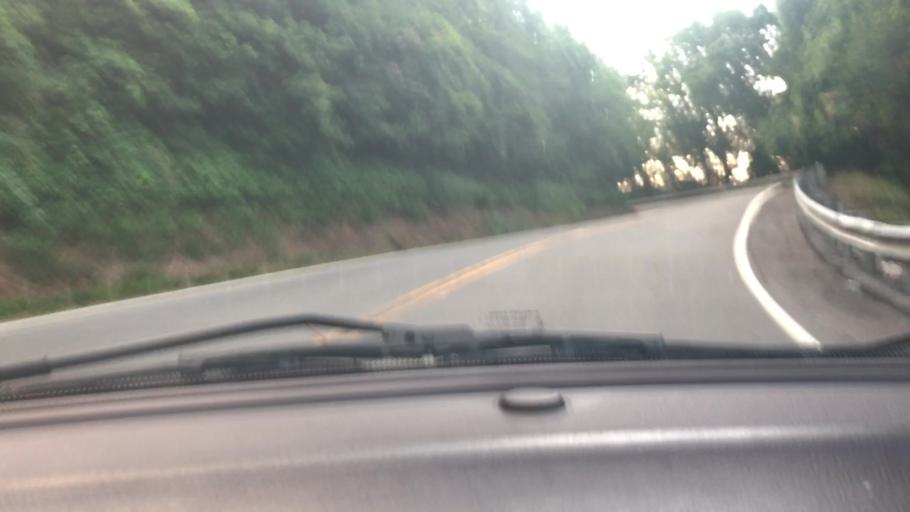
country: US
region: Virginia
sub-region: Patrick County
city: Stuart
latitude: 36.7200
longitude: -80.3312
